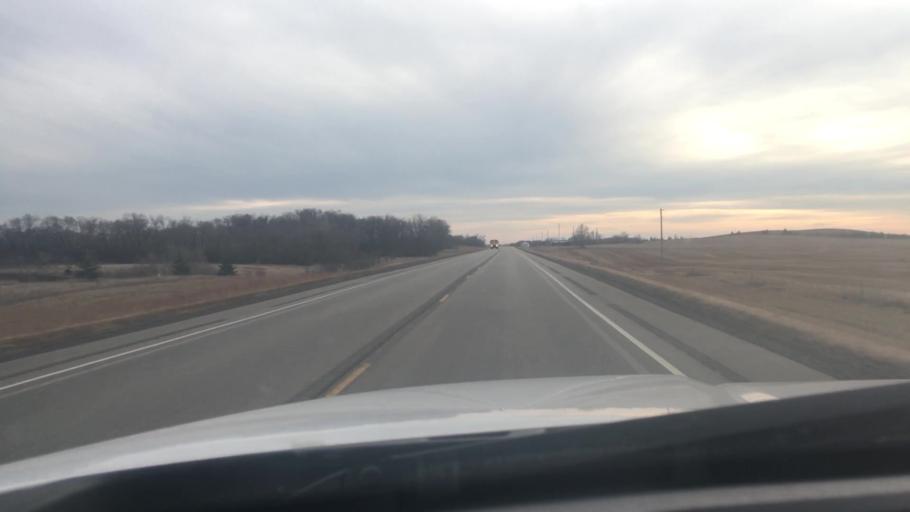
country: US
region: Minnesota
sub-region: Otter Tail County
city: Perham
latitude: 46.3327
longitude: -95.7185
